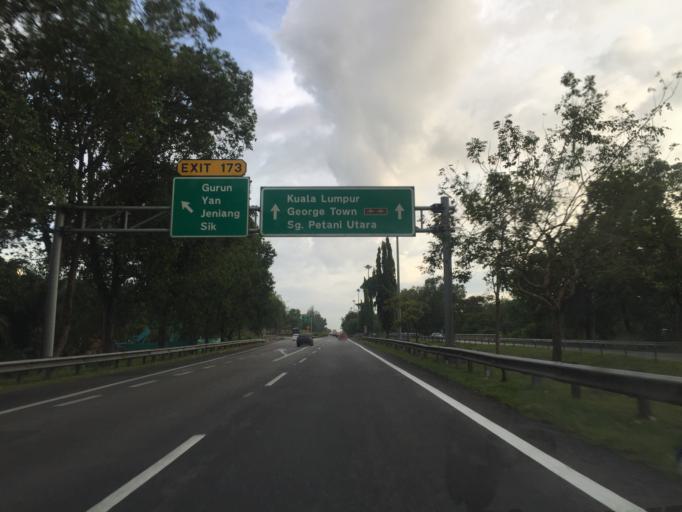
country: MY
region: Kedah
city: Gurun
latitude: 5.8195
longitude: 100.4902
